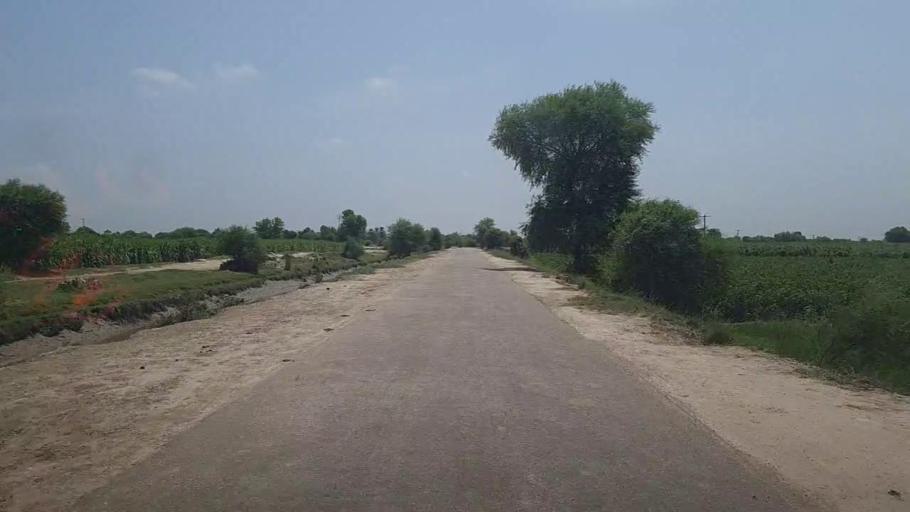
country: PK
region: Sindh
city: Ubauro
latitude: 28.2923
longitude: 69.8069
